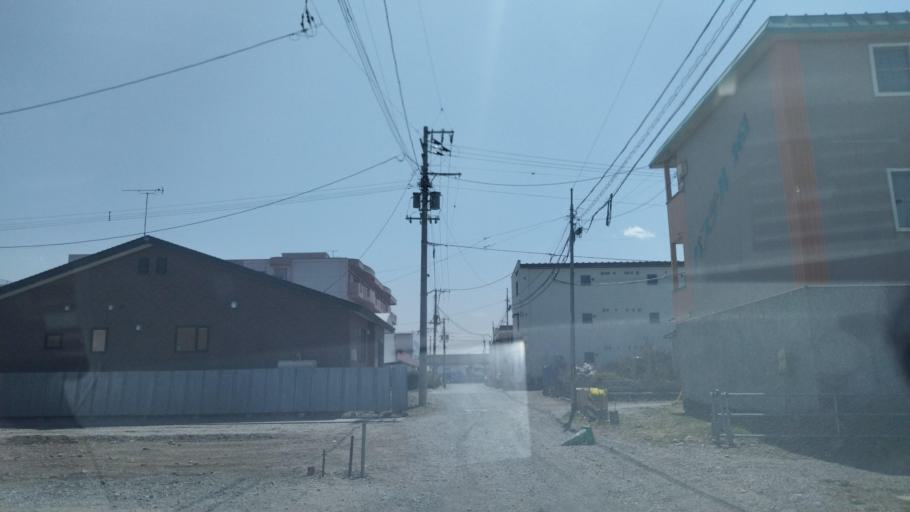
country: JP
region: Hokkaido
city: Obihiro
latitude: 42.9314
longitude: 143.1749
